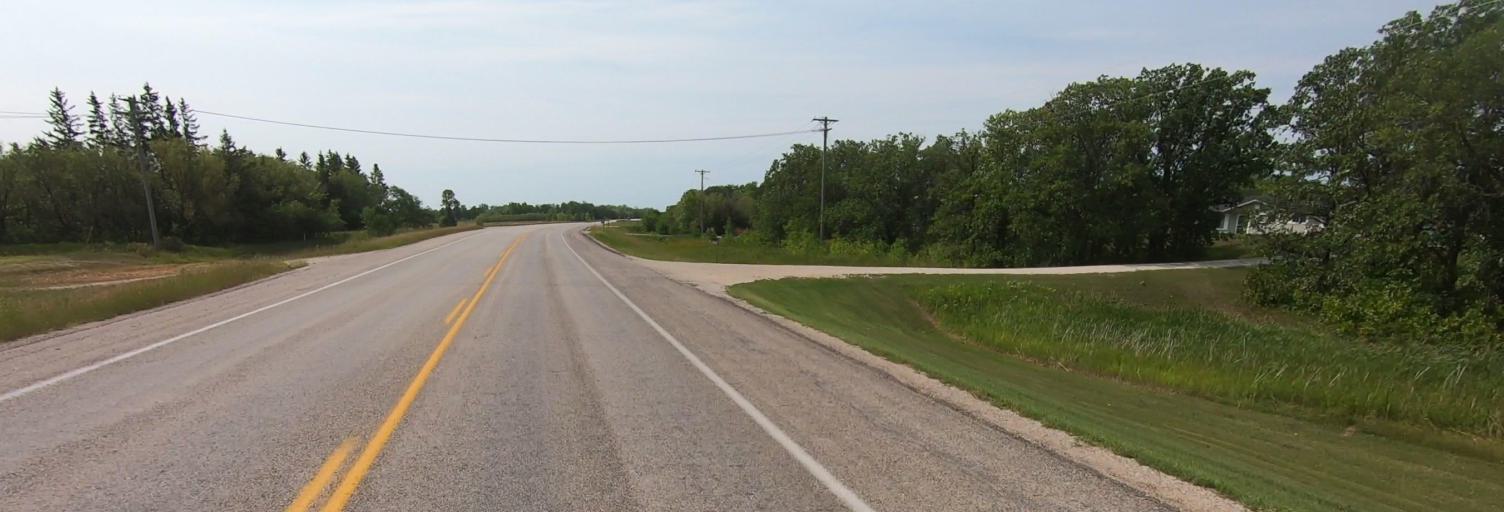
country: CA
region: Manitoba
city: Niverville
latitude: 49.6379
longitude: -97.1065
